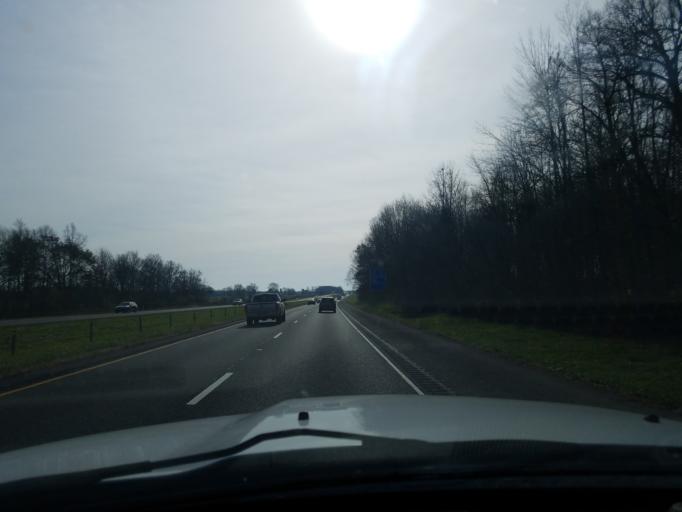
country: US
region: Indiana
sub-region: Delaware County
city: Daleville
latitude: 40.1484
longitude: -85.5673
